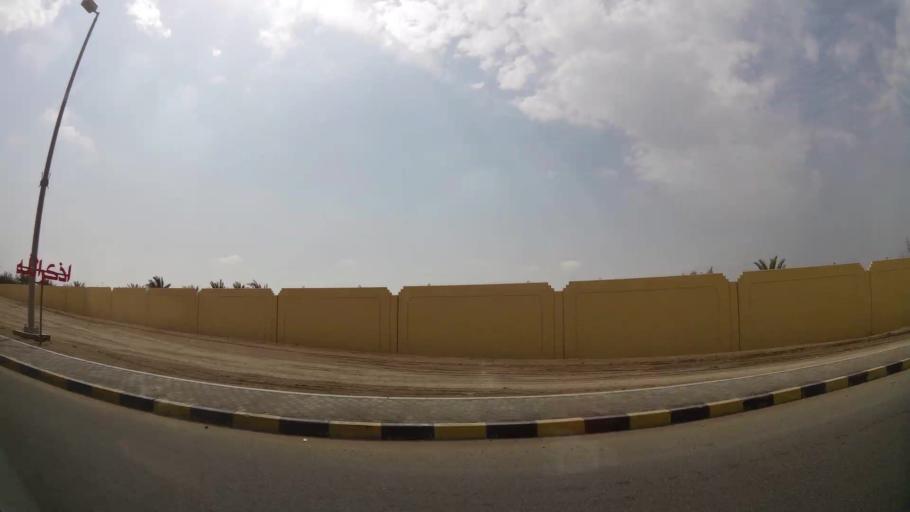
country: AE
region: Abu Dhabi
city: Abu Dhabi
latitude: 24.5146
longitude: 54.6594
